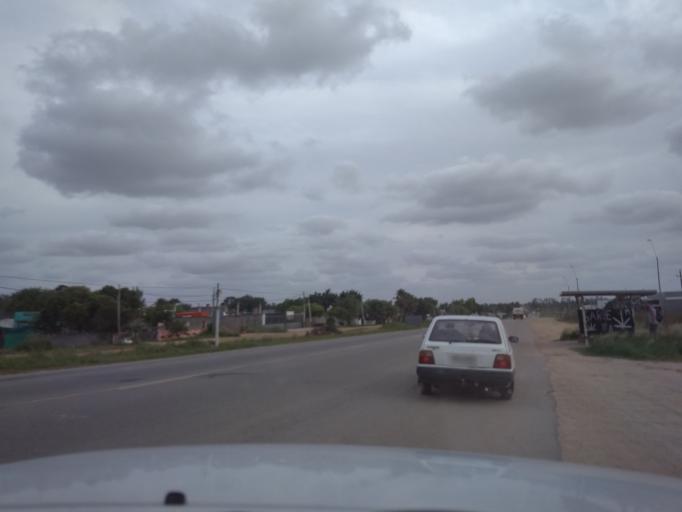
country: UY
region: Canelones
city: Colonia Nicolich
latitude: -34.7870
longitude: -56.0009
